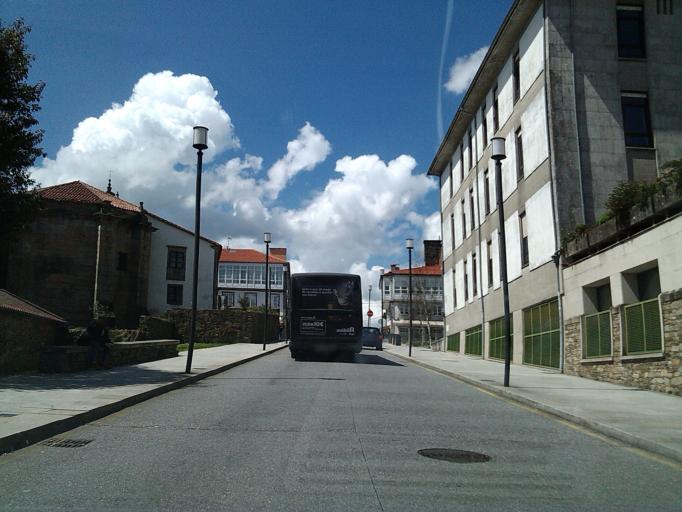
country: ES
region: Galicia
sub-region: Provincia da Coruna
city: Santiago de Compostela
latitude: 42.8835
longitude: -8.5412
